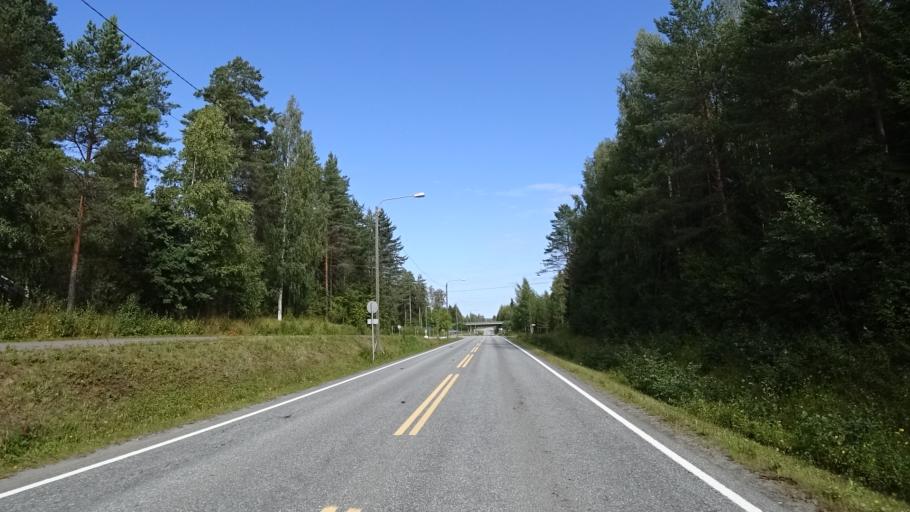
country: FI
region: North Karelia
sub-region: Joensuu
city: Pyhaeselkae
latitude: 62.4749
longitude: 29.9535
